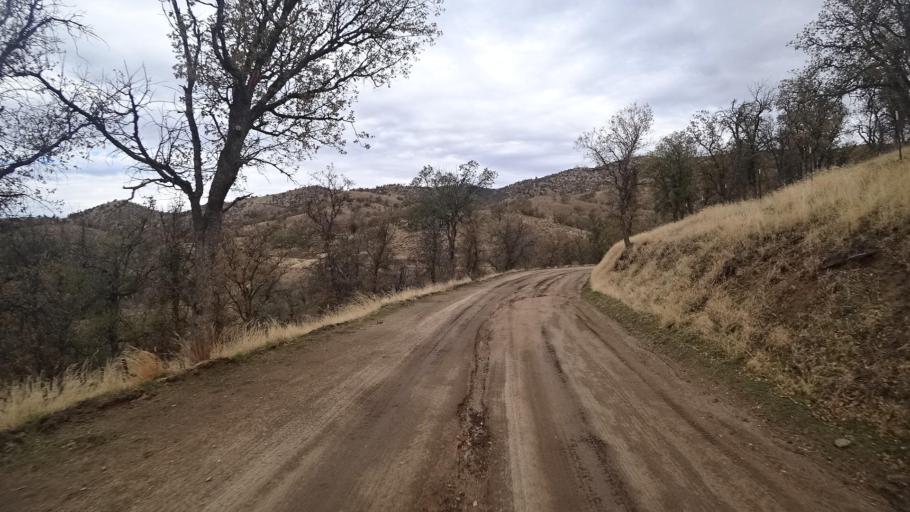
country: US
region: California
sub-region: Kern County
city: Stallion Springs
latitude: 35.1159
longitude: -118.6958
